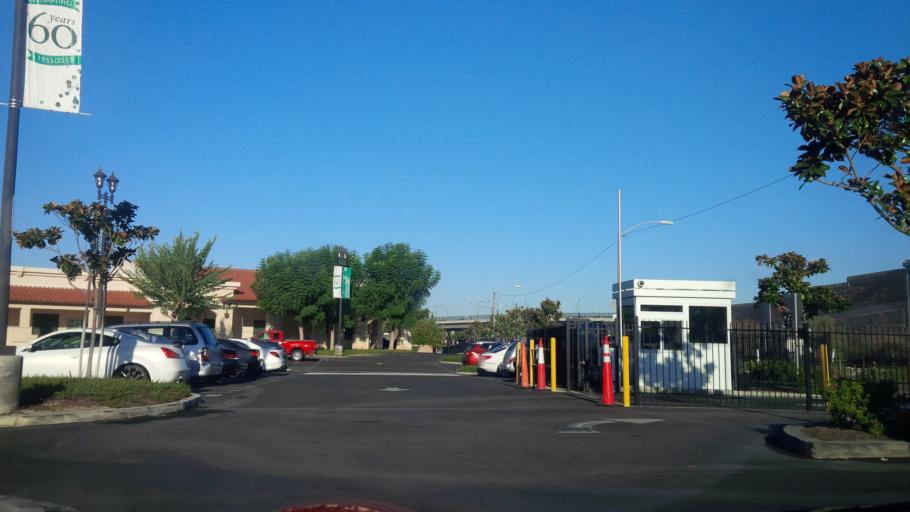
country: US
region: California
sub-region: Orange County
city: Fullerton
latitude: 33.8446
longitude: -117.9597
